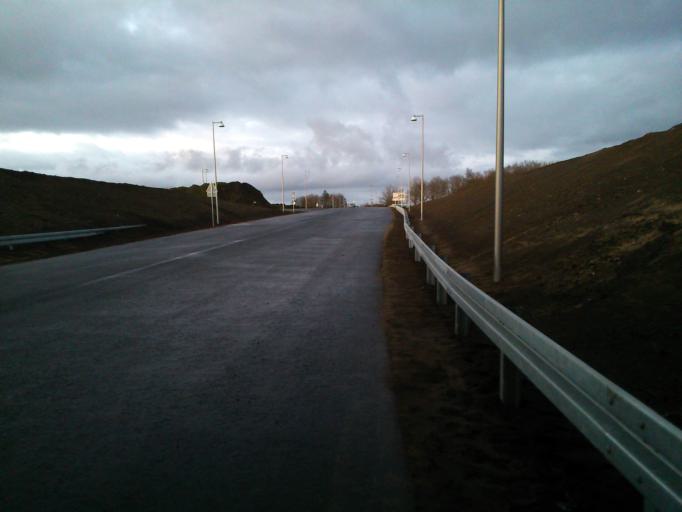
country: DK
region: Central Jutland
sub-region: Herning Kommune
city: Avlum
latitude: 56.2549
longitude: 8.7836
